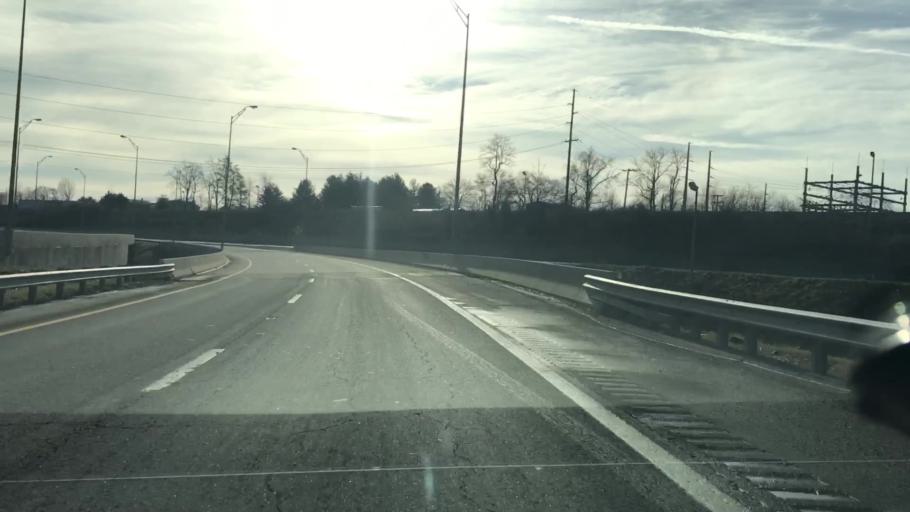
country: US
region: Virginia
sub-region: Montgomery County
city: Christiansburg
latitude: 37.1538
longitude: -80.4115
